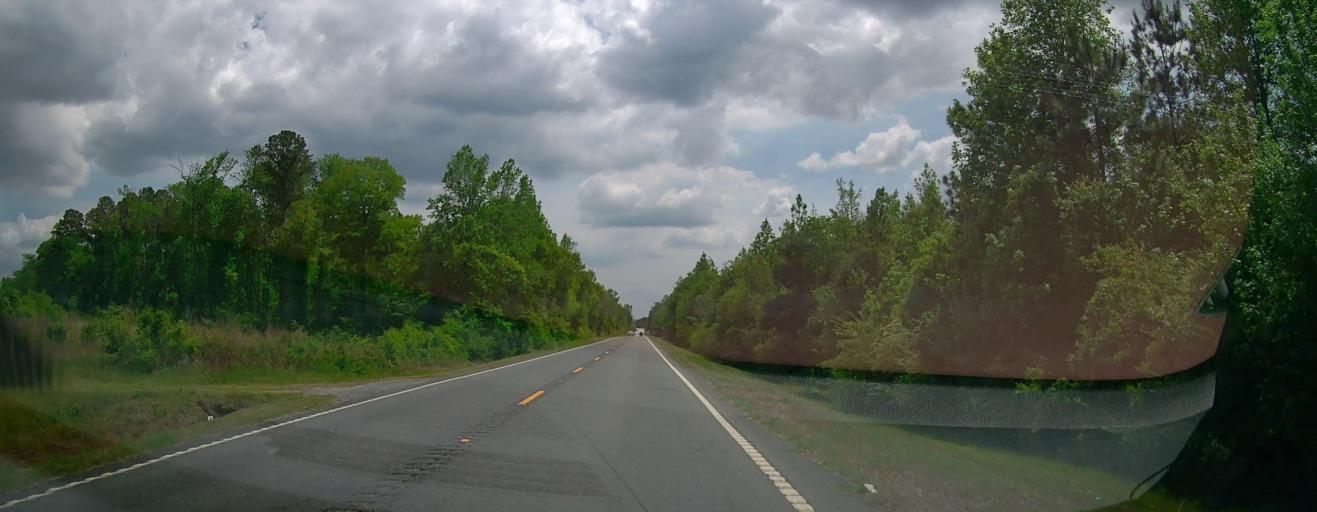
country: US
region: Georgia
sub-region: Treutlen County
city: Soperton
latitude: 32.3938
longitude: -82.6012
